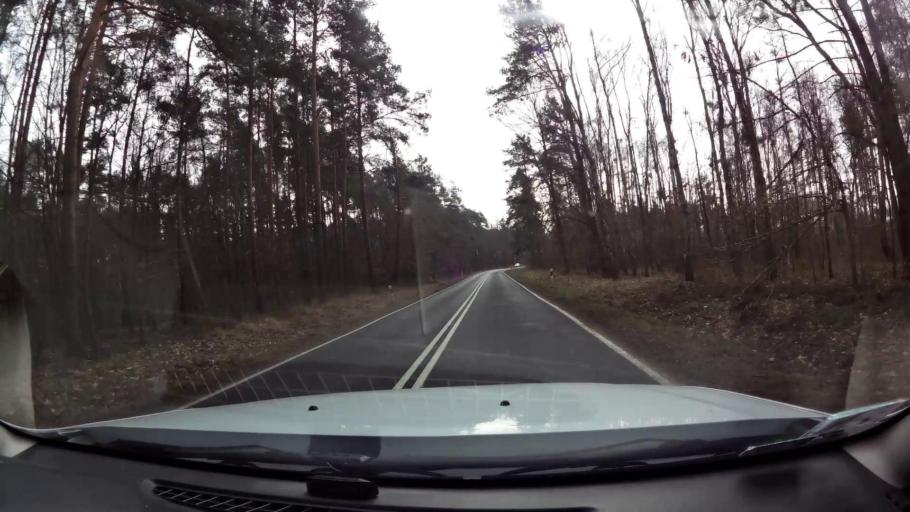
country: PL
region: West Pomeranian Voivodeship
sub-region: Powiat mysliborski
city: Debno
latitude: 52.7580
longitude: 14.6842
